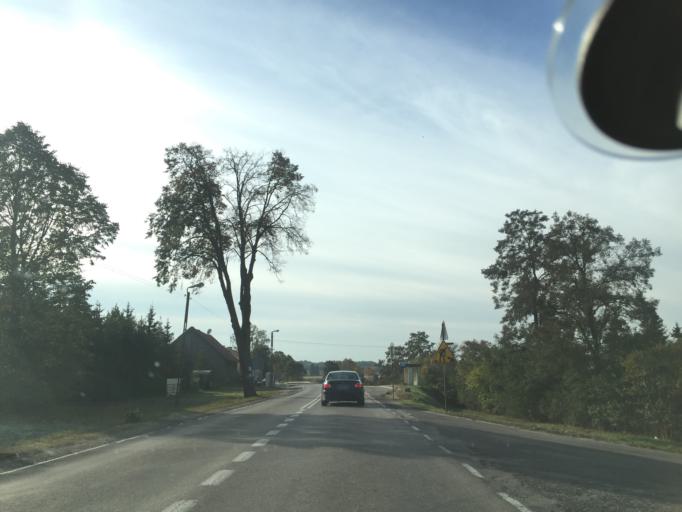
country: PL
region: Warmian-Masurian Voivodeship
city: Dobre Miasto
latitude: 54.0268
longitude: 20.4100
